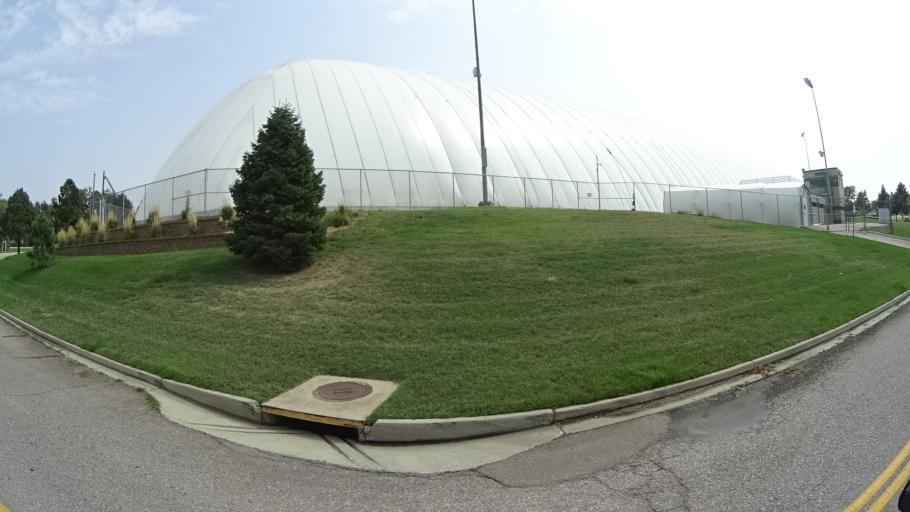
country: US
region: Colorado
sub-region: El Paso County
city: Colorado Springs
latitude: 38.8299
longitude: -104.7963
